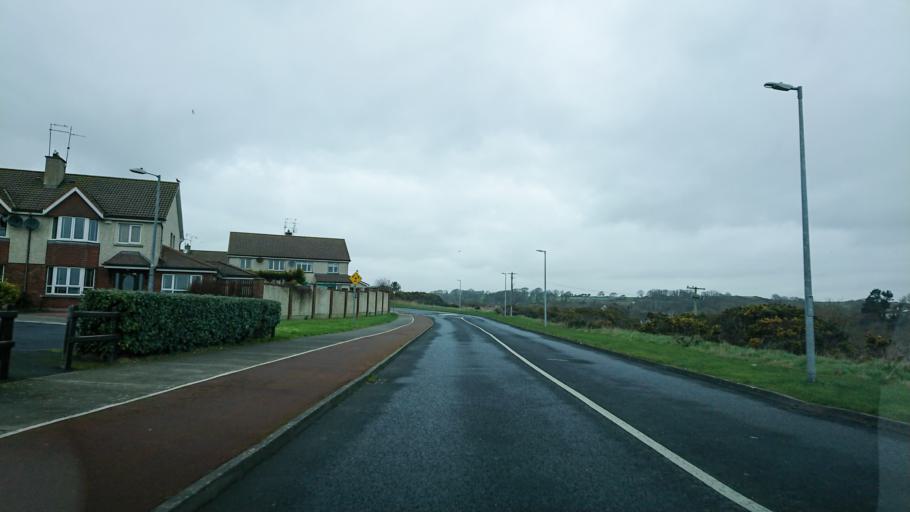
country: IE
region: Munster
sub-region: Waterford
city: Tra Mhor
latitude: 52.1712
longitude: -7.1361
